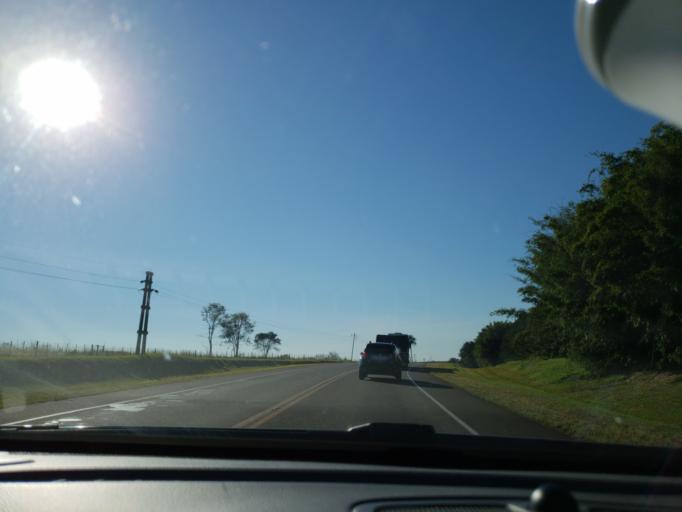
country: AR
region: Misiones
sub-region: Departamento de Apostoles
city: San Jose
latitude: -27.6670
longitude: -55.8155
